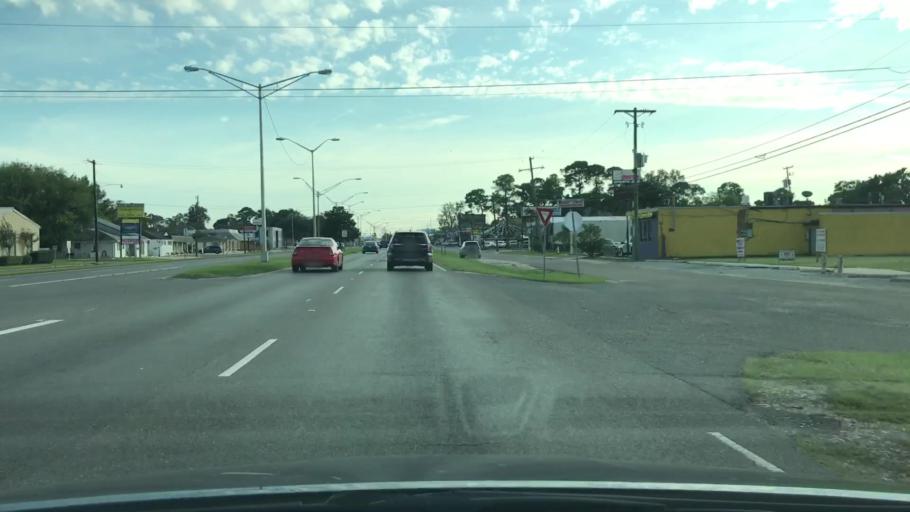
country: US
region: Louisiana
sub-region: Jefferson Parish
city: Metairie
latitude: 29.9855
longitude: -90.1561
